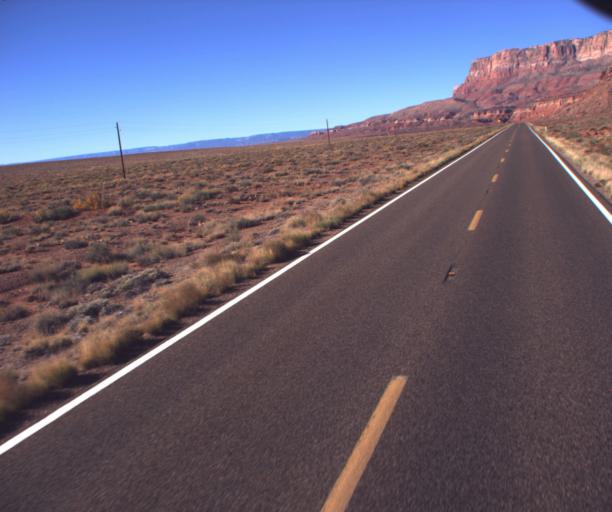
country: US
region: Arizona
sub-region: Coconino County
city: Page
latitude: 36.7520
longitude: -111.7240
